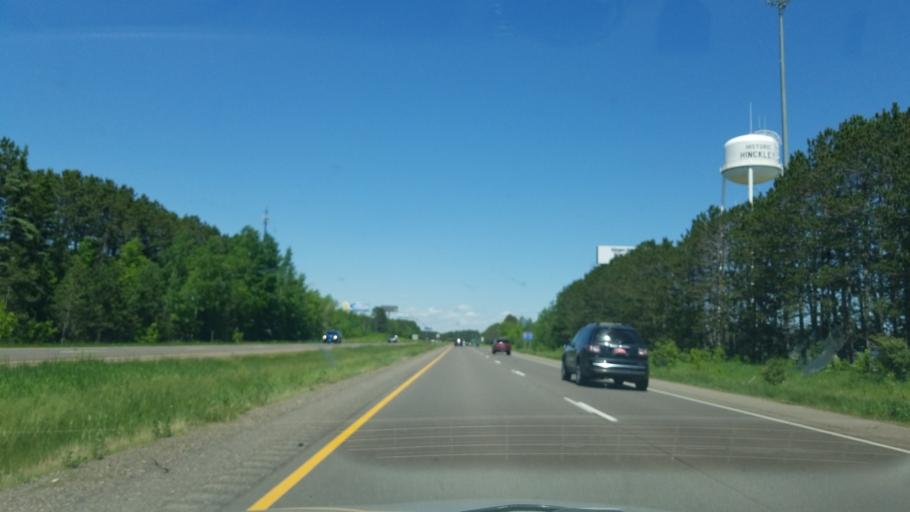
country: US
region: Minnesota
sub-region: Pine County
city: Hinckley
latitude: 46.0164
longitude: -92.9292
